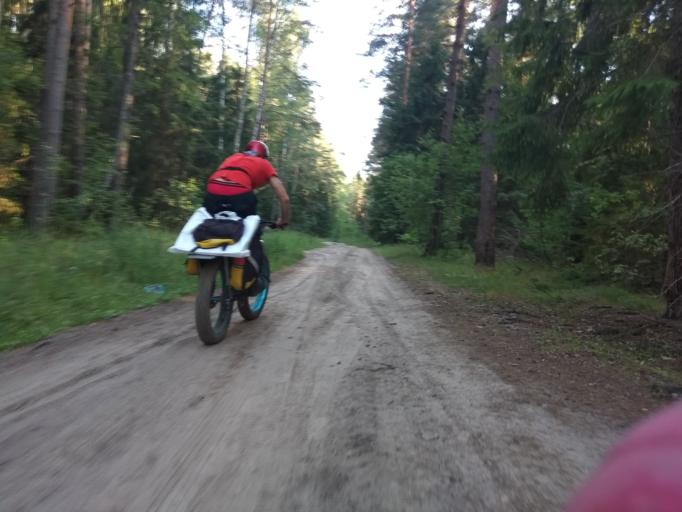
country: RU
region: Moskovskaya
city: Misheronskiy
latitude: 55.7348
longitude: 39.7691
